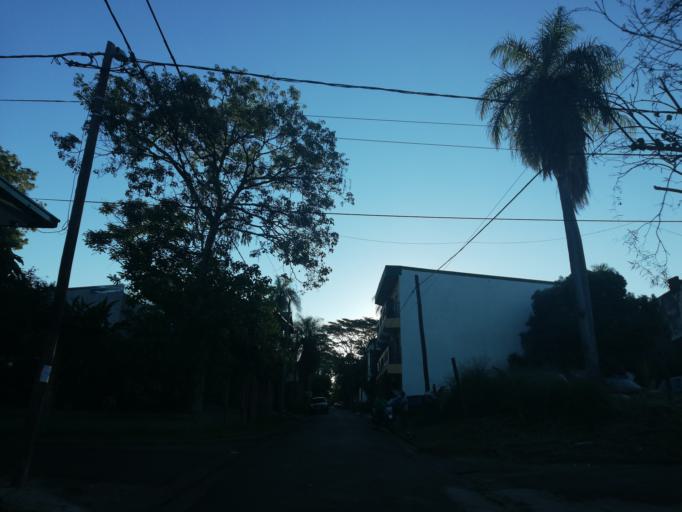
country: AR
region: Misiones
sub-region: Departamento de Capital
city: Posadas
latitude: -27.3870
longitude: -55.8907
